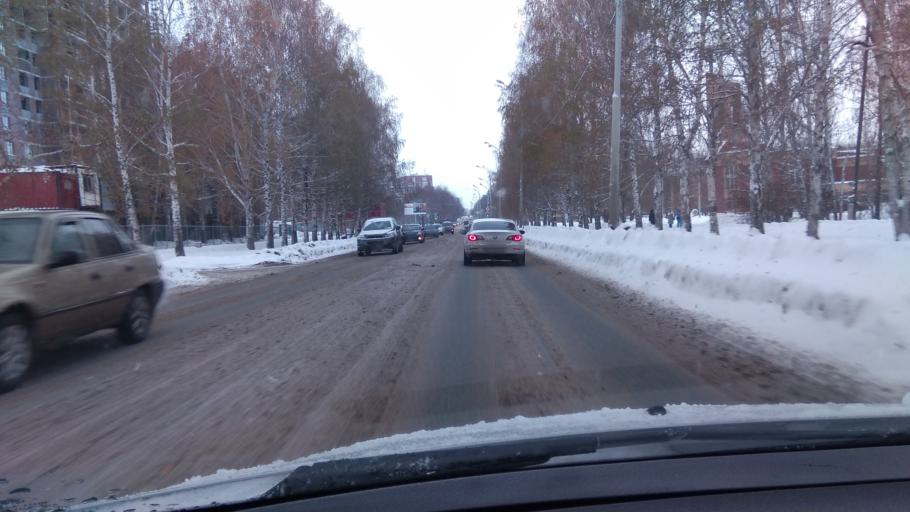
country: RU
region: Sverdlovsk
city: Yekaterinburg
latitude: 56.8134
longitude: 60.5734
